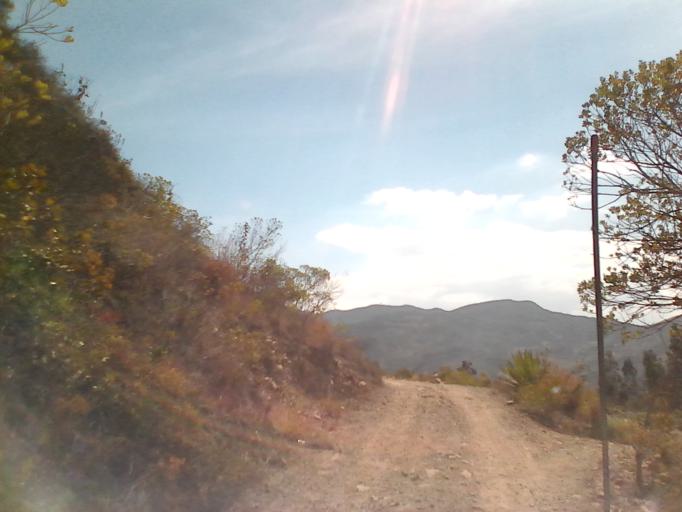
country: CO
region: Boyaca
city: Sachica
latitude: 5.5478
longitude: -73.5222
